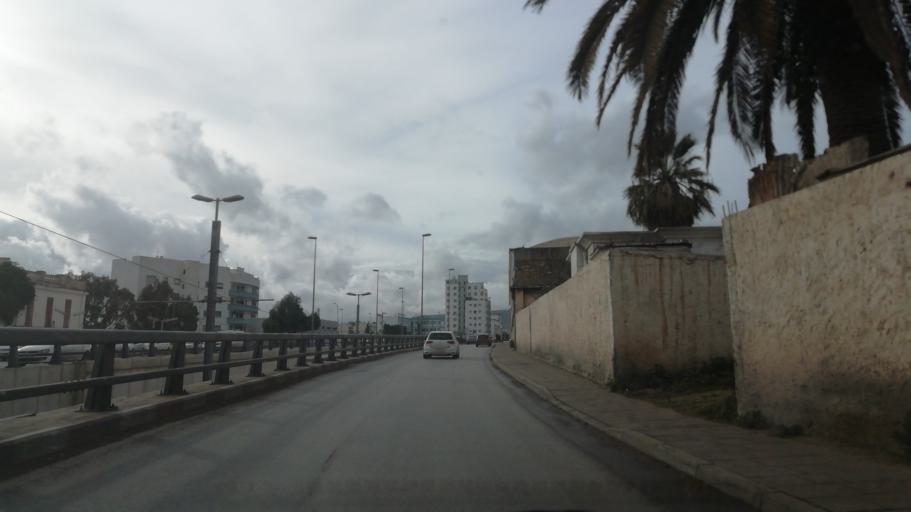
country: DZ
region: Oran
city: Oran
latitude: 35.6969
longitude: -0.6113
